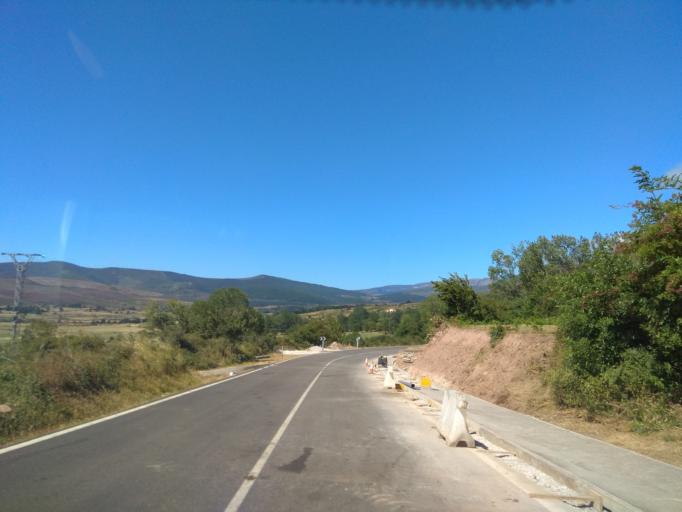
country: ES
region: Cantabria
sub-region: Provincia de Cantabria
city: Villaescusa
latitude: 42.9386
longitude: -4.1811
